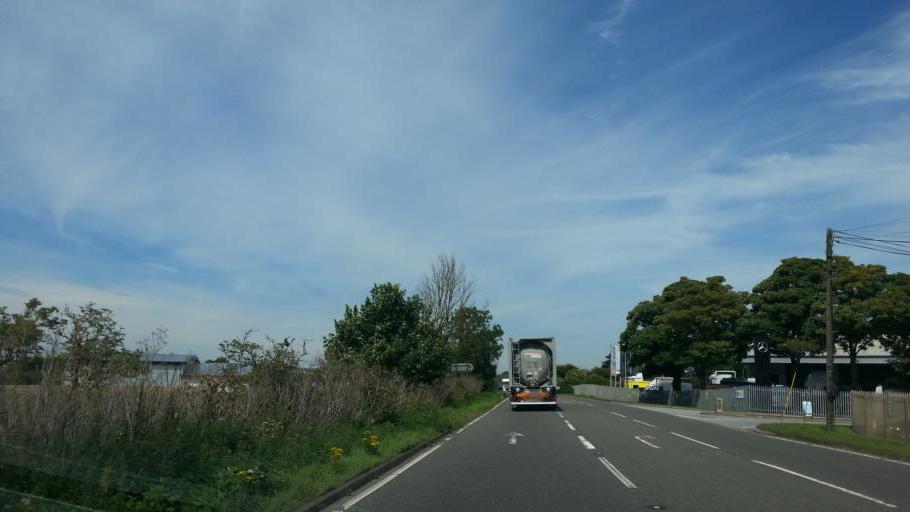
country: GB
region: England
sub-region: Suffolk
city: Exning
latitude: 52.2852
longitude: 0.3934
